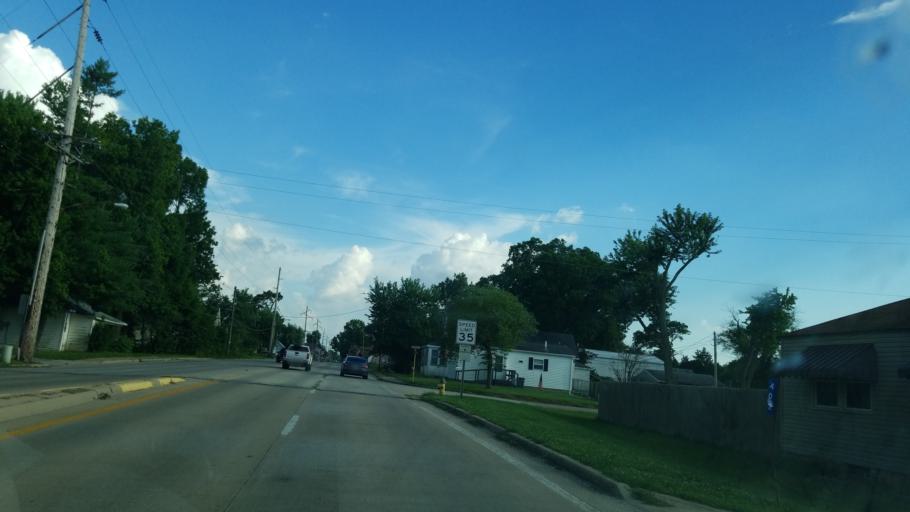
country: US
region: Illinois
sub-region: Marion County
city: Central City
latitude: 38.5533
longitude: -89.1294
